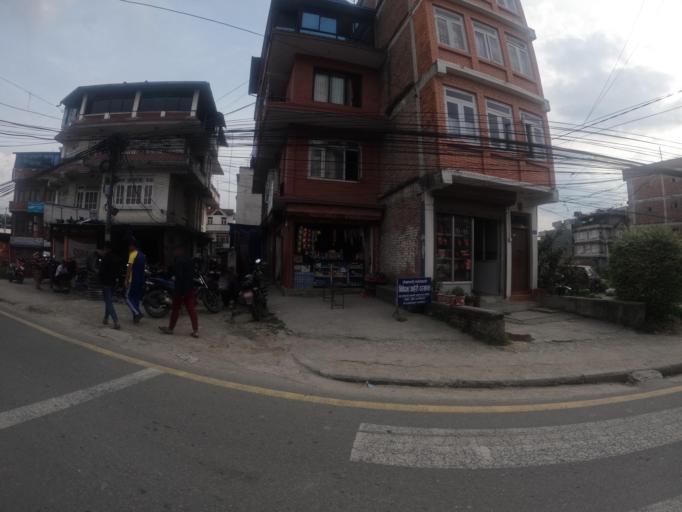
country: NP
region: Central Region
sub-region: Bagmati Zone
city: Bhaktapur
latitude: 27.6820
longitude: 85.3914
